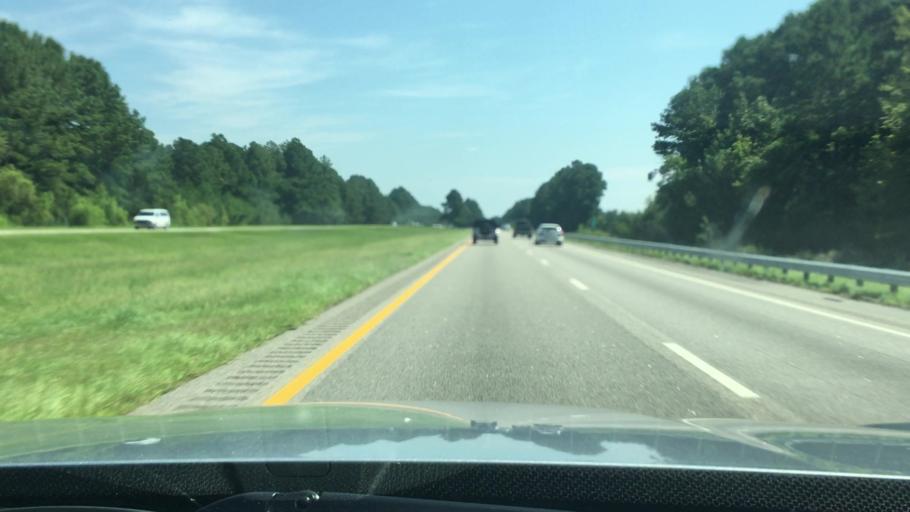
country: US
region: South Carolina
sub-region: Florence County
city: Timmonsville
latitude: 33.9822
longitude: -80.0309
